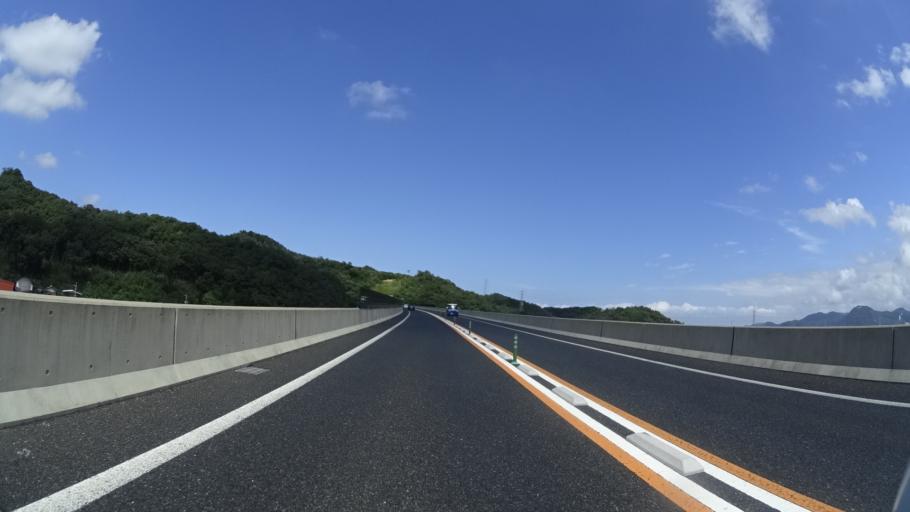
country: JP
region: Tottori
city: Tottori
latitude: 35.4850
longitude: 134.1980
